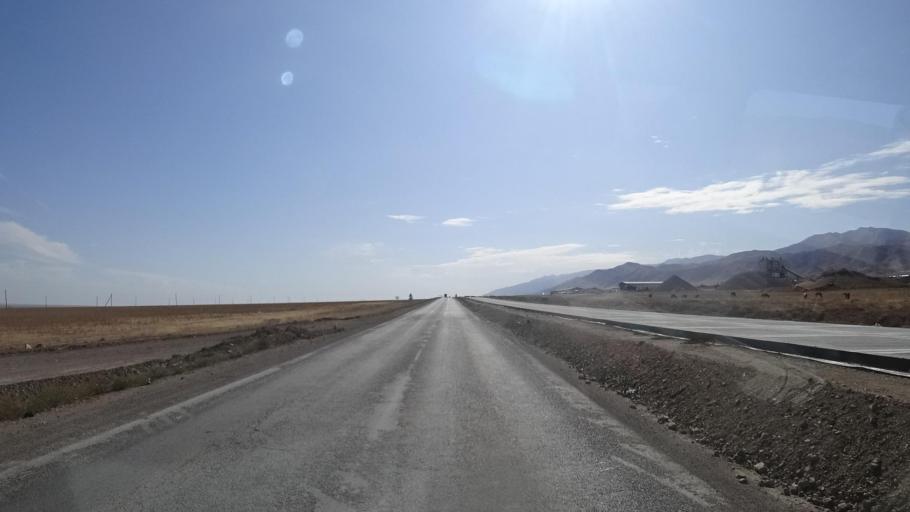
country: KG
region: Chuy
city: Ivanovka
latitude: 43.3919
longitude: 75.1379
